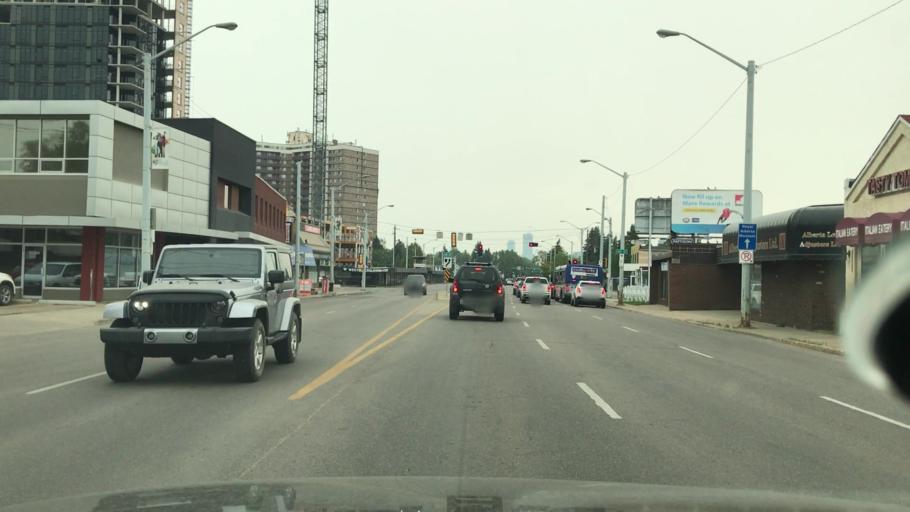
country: CA
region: Alberta
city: Edmonton
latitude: 53.5428
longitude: -113.5674
